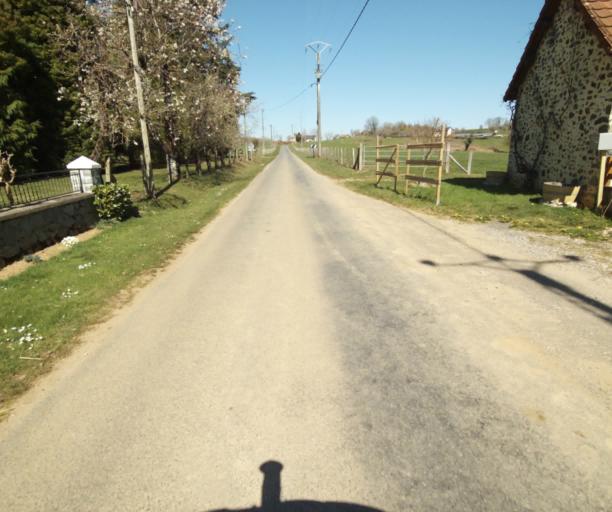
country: FR
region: Limousin
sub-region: Departement de la Correze
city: Saint-Clement
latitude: 45.3348
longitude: 1.7067
